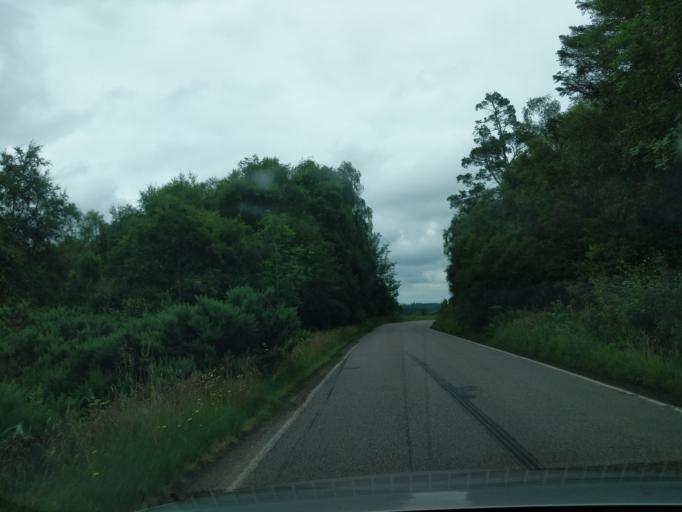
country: GB
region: Scotland
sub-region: Moray
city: Forres
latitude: 57.5150
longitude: -3.6916
